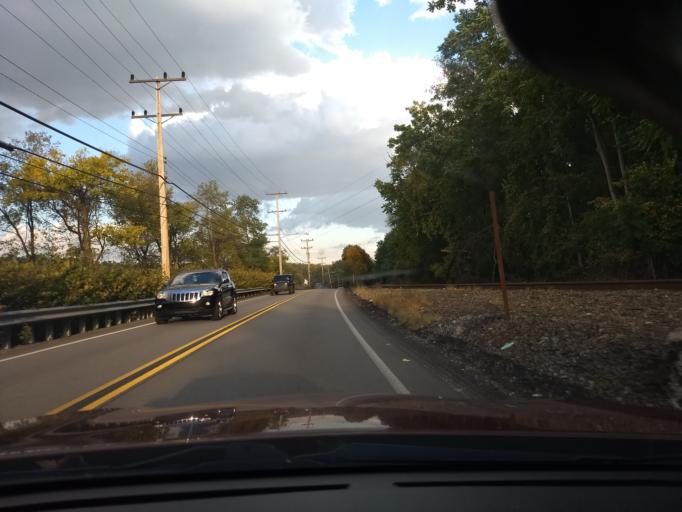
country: US
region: Pennsylvania
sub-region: Allegheny County
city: Dravosburg
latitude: 40.3659
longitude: -79.8956
